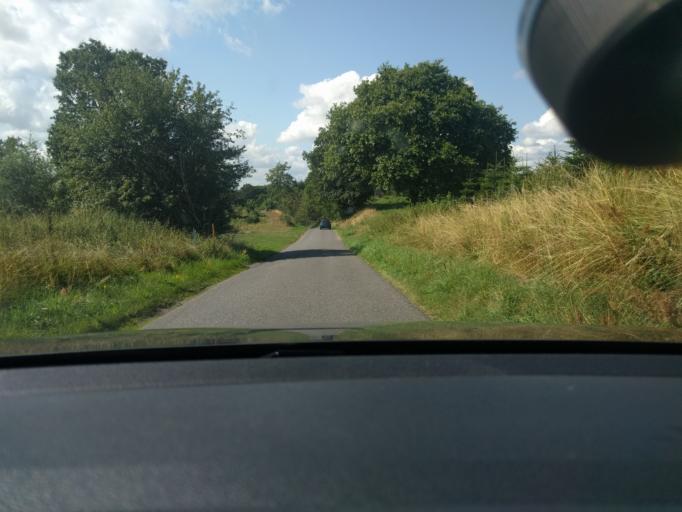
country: DK
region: Central Jutland
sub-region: Viborg Kommune
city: Bjerringbro
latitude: 56.4659
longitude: 9.5965
